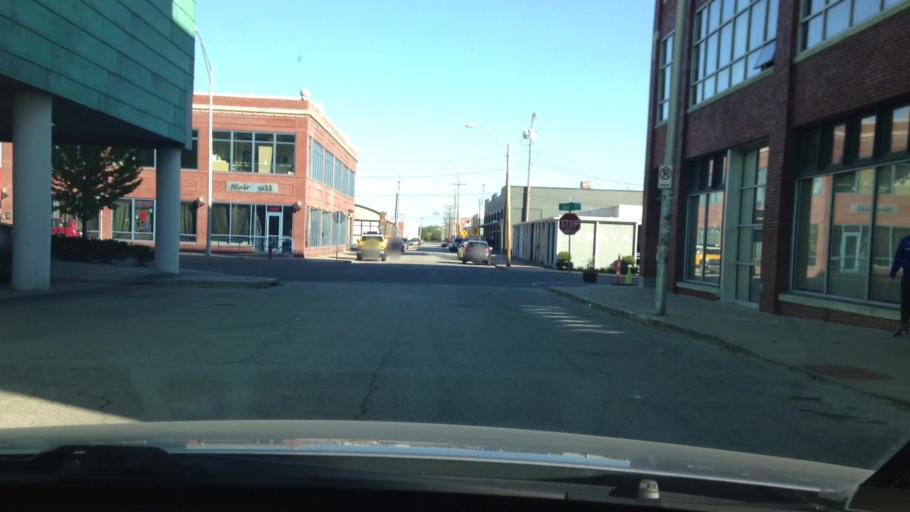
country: US
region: Missouri
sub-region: Jackson County
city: Kansas City
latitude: 39.0934
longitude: -94.5794
